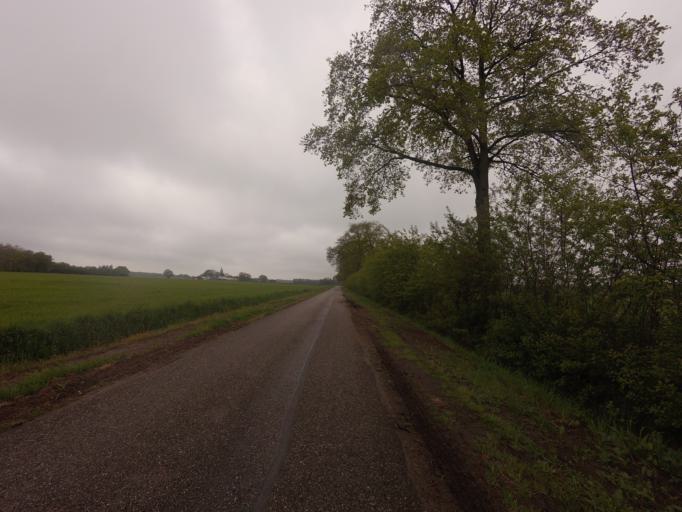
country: NL
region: Overijssel
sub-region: Gemeente Haaksbergen
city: Haaksbergen
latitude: 52.1414
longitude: 6.8056
